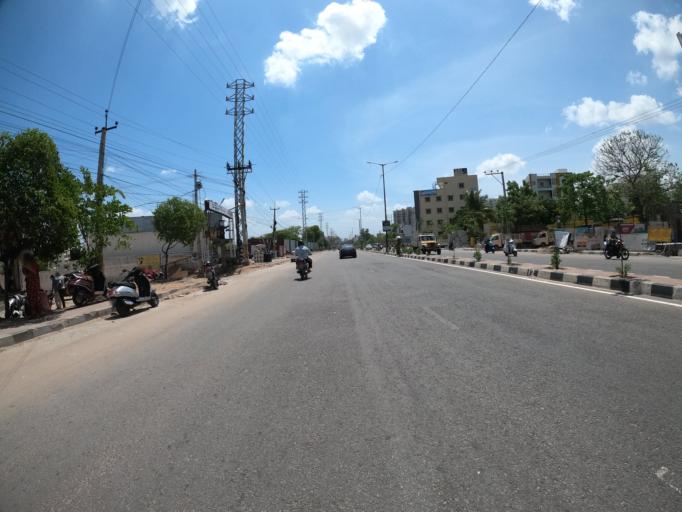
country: IN
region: Telangana
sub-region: Hyderabad
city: Hyderabad
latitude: 17.3555
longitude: 78.3803
